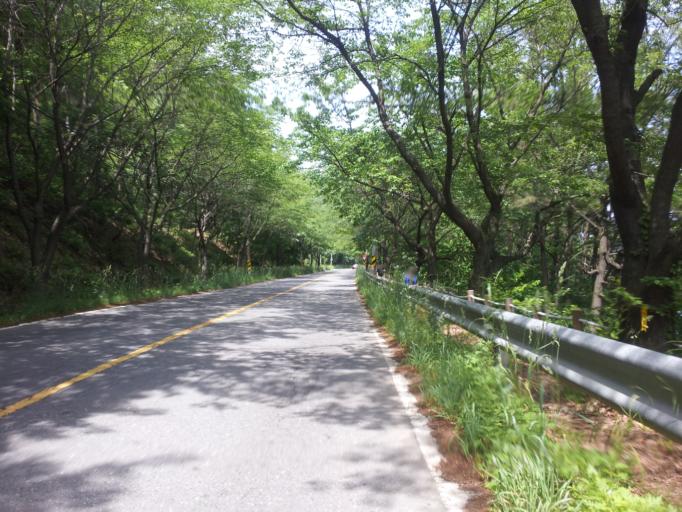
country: KR
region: Daejeon
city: Sintansin
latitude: 36.4347
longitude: 127.4697
